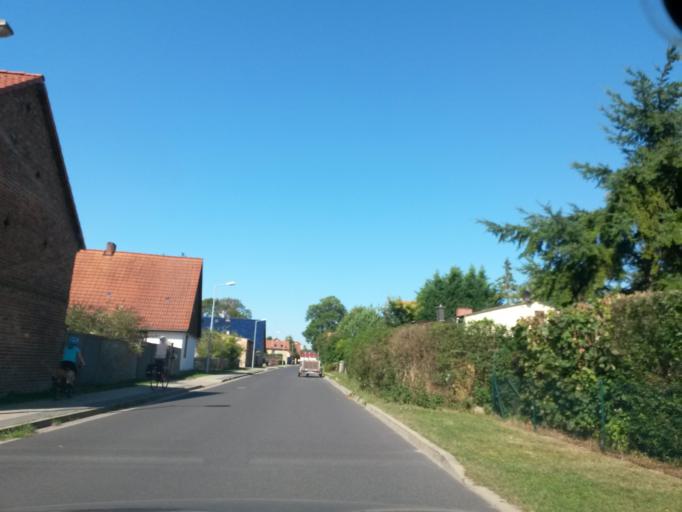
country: DE
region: Brandenburg
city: Prenzlau
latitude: 53.2160
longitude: 13.8458
